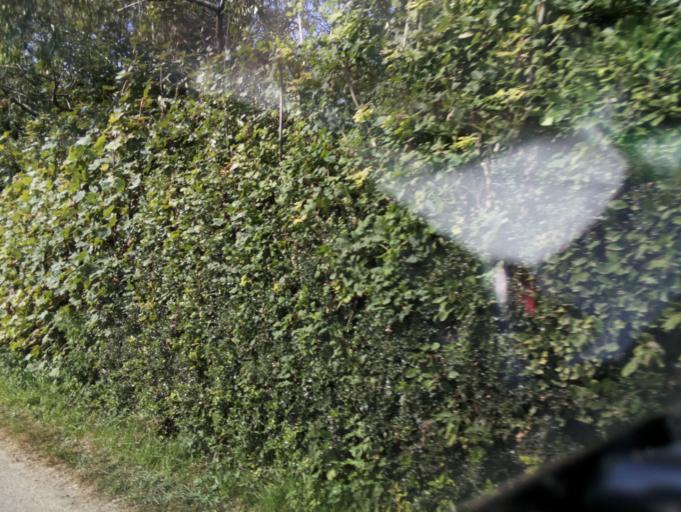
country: GB
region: England
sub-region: Gloucestershire
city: Dursley
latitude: 51.7058
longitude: -2.3145
